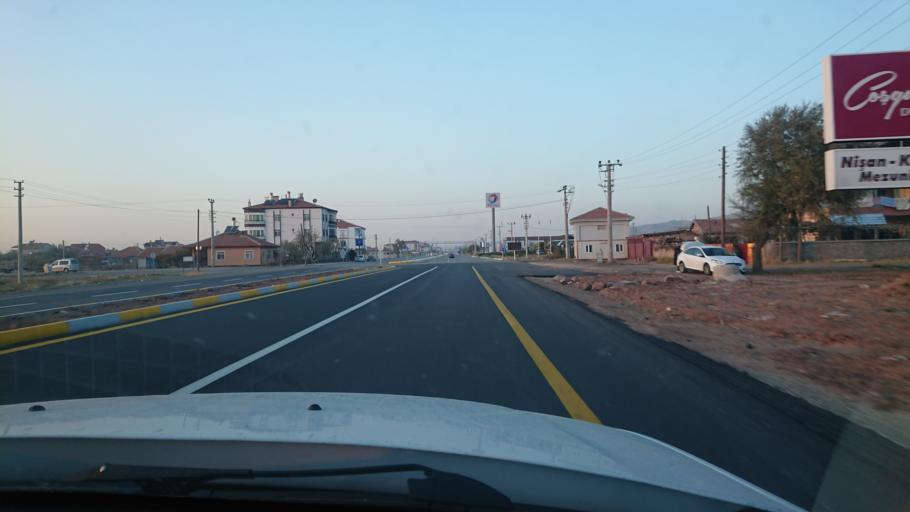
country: TR
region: Aksaray
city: Aksaray
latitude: 38.3306
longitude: 34.0507
